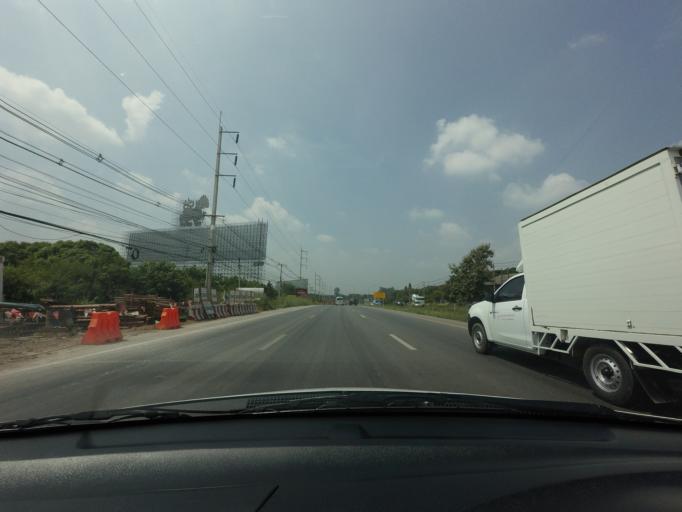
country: TH
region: Nakhon Ratchasima
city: Pak Chong
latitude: 14.6521
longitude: 101.3562
